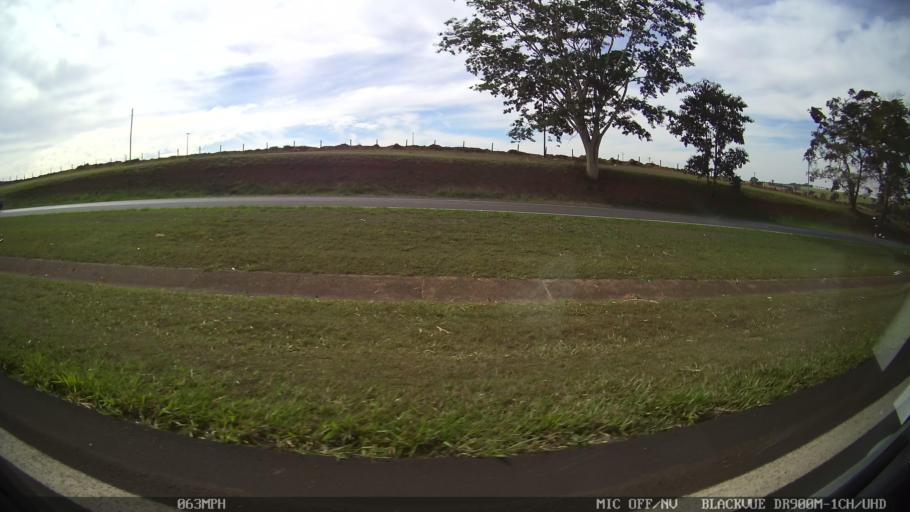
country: BR
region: Sao Paulo
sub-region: Matao
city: Matao
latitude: -21.5616
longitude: -48.4738
